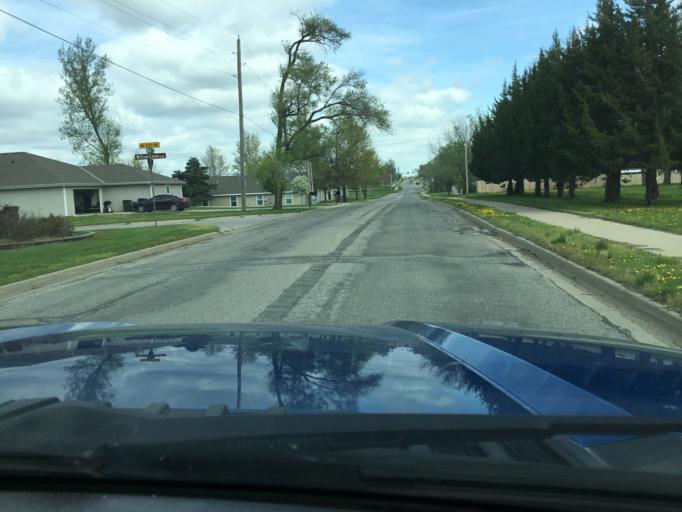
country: US
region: Kansas
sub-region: Douglas County
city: Lawrence
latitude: 38.9392
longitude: -95.2142
